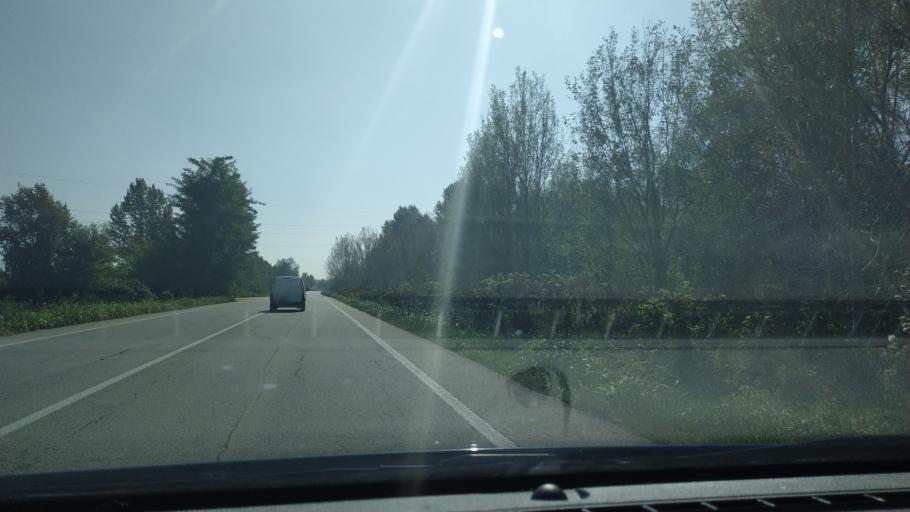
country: IT
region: Piedmont
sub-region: Provincia di Alessandria
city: Valenza
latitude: 45.0394
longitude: 8.6239
